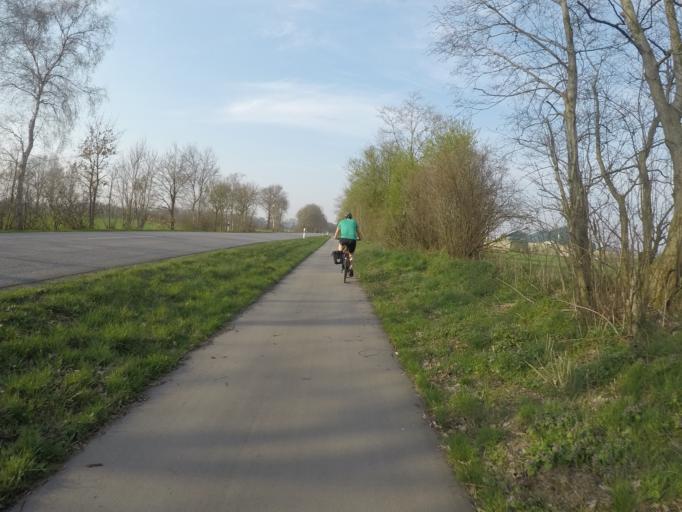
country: DE
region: Schleswig-Holstein
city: Wahlstedt
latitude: 53.9724
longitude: 10.1877
